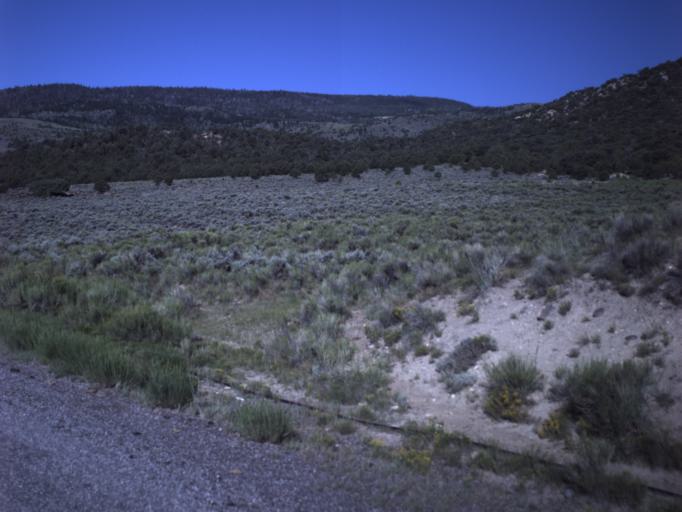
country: US
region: Utah
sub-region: Wayne County
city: Loa
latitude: 38.6274
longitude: -111.4474
